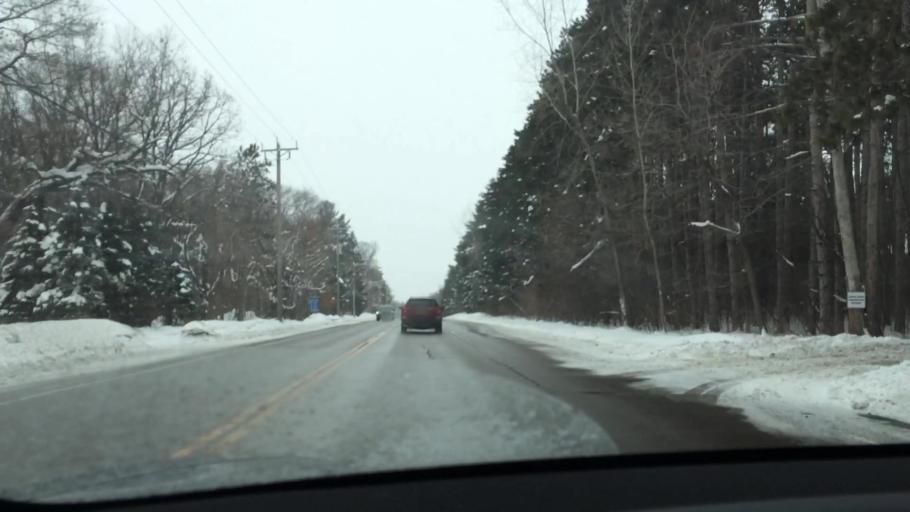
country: US
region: Minnesota
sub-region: Ramsey County
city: Shoreview
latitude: 45.0981
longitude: -93.1272
